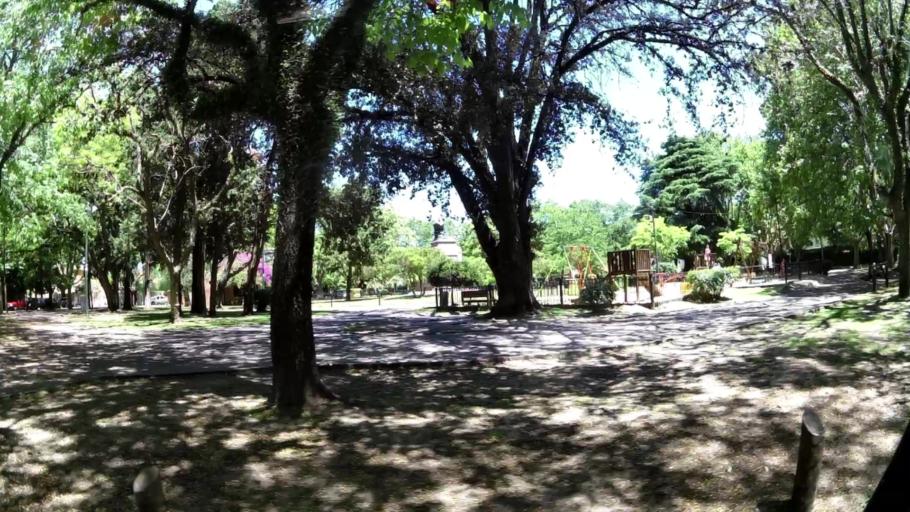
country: AR
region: Buenos Aires
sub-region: Partido de San Isidro
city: San Isidro
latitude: -34.4742
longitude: -58.5063
